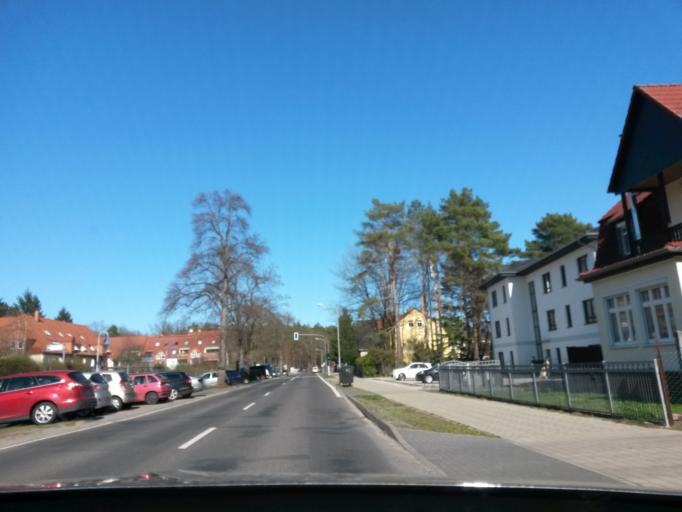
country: DE
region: Brandenburg
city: Grunheide
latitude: 52.4340
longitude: 13.8346
